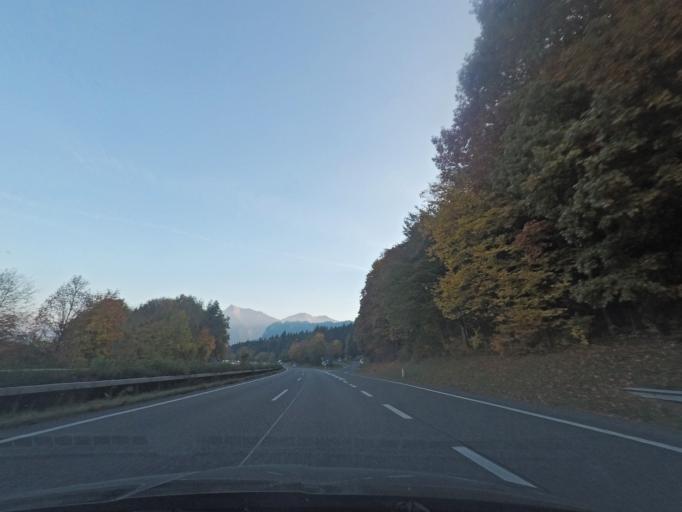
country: CH
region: Bern
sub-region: Thun District
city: Thun
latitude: 46.7349
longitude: 7.6007
